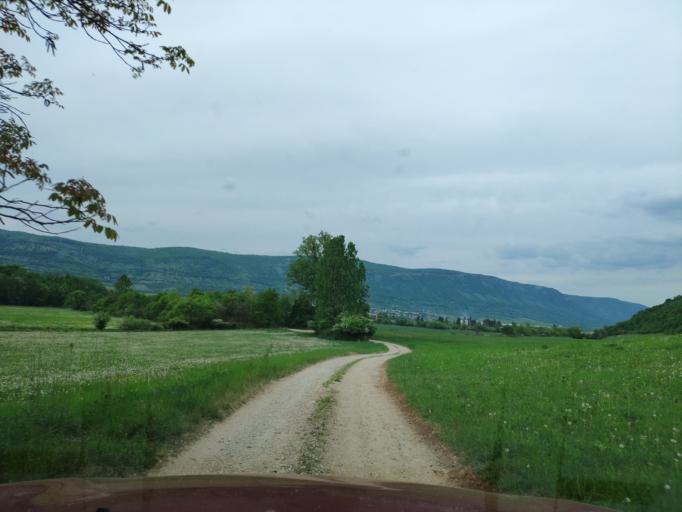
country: SK
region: Kosicky
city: Roznava
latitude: 48.5726
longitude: 20.6508
